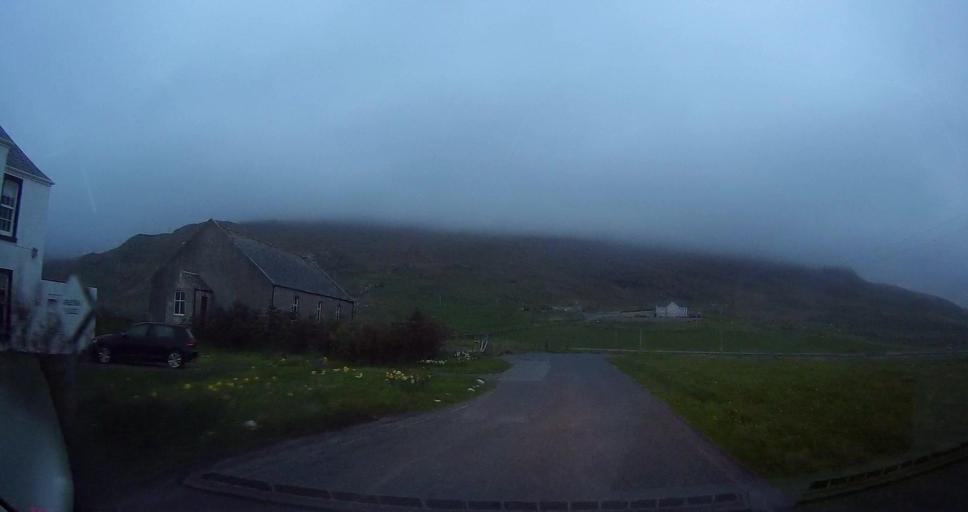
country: GB
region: Scotland
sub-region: Shetland Islands
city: Sandwick
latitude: 60.0346
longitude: -1.2294
